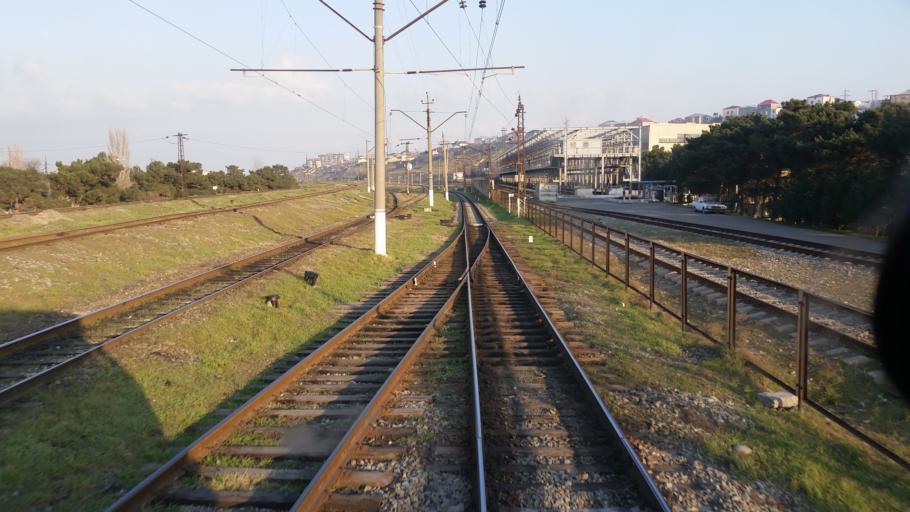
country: AZ
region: Baki
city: Bilajari
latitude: 40.4347
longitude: 49.8183
